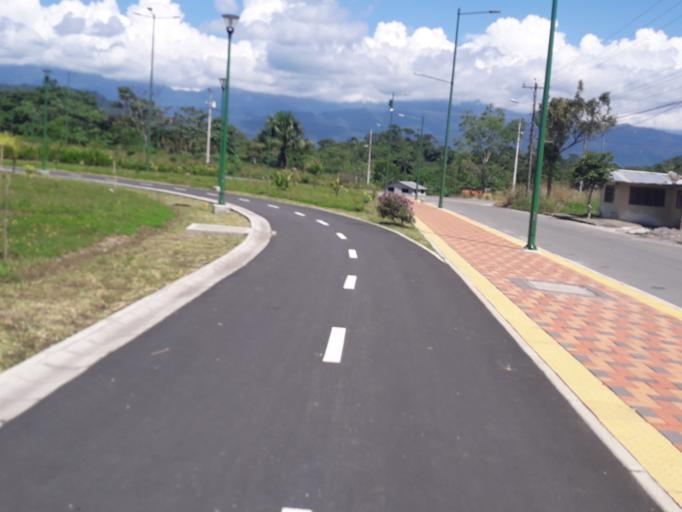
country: EC
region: Napo
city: Tena
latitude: -0.9852
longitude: -77.8236
